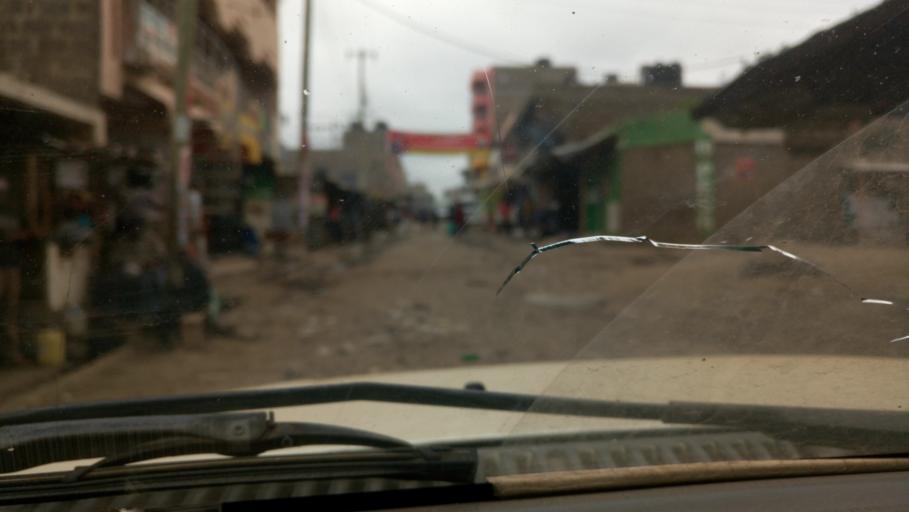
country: KE
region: Nairobi Area
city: Pumwani
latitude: -1.2558
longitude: 36.9245
